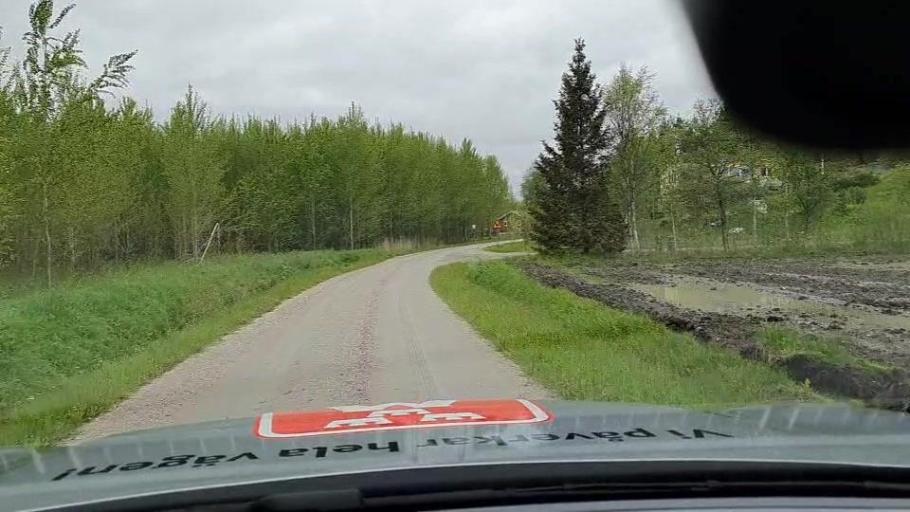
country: SE
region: Soedermanland
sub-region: Nykopings Kommun
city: Svalsta
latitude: 58.6218
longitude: 16.9379
